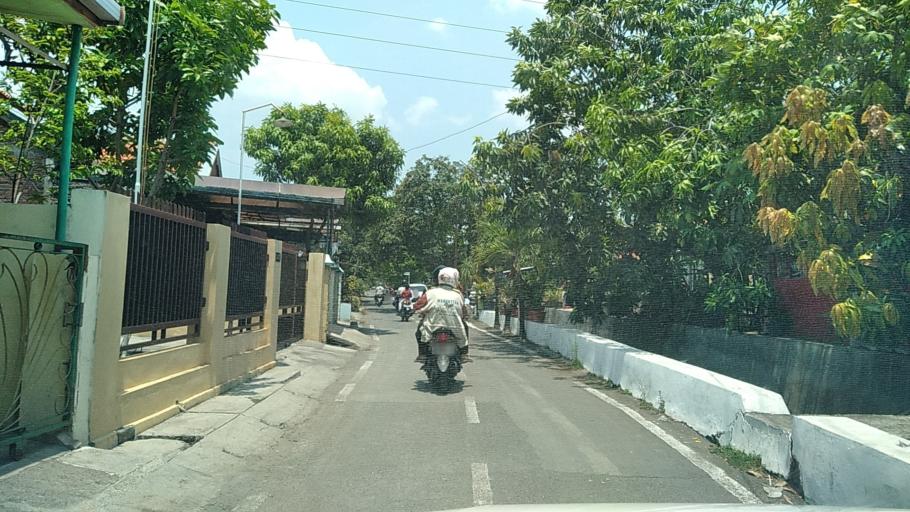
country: ID
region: Central Java
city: Semarang
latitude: -7.0050
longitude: 110.4483
